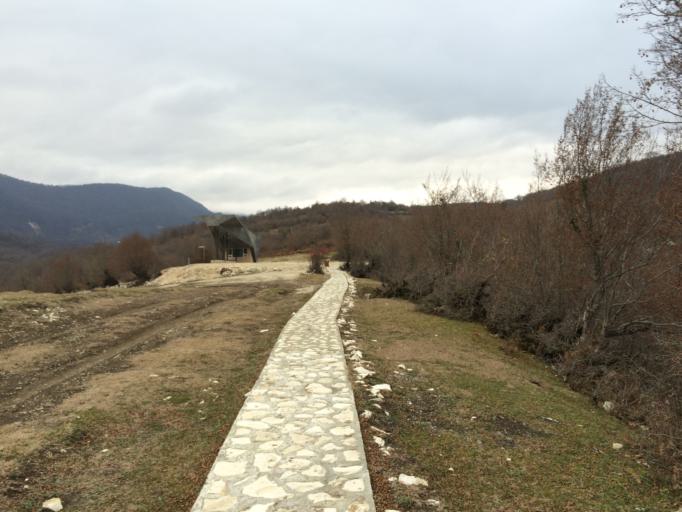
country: GE
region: Imereti
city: Tsqaltubo
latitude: 42.4539
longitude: 42.5494
